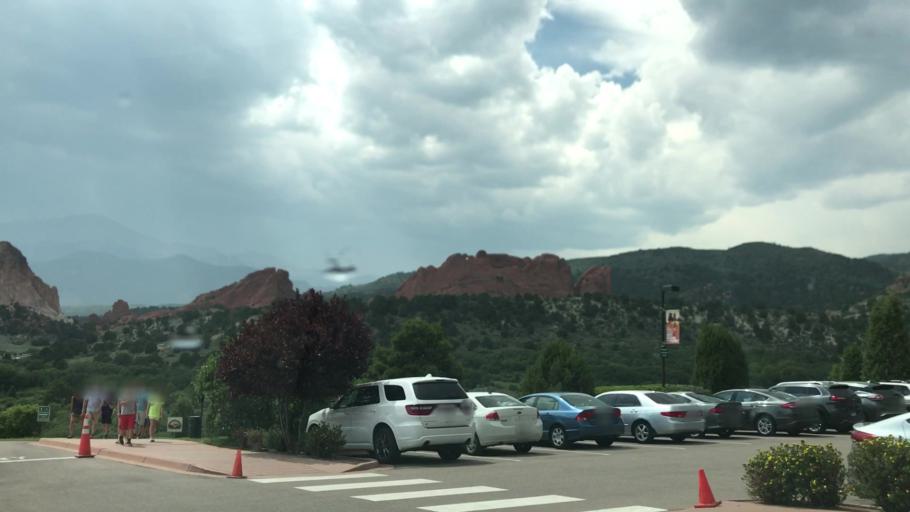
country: US
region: Colorado
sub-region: El Paso County
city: Manitou Springs
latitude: 38.8784
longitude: -104.8702
